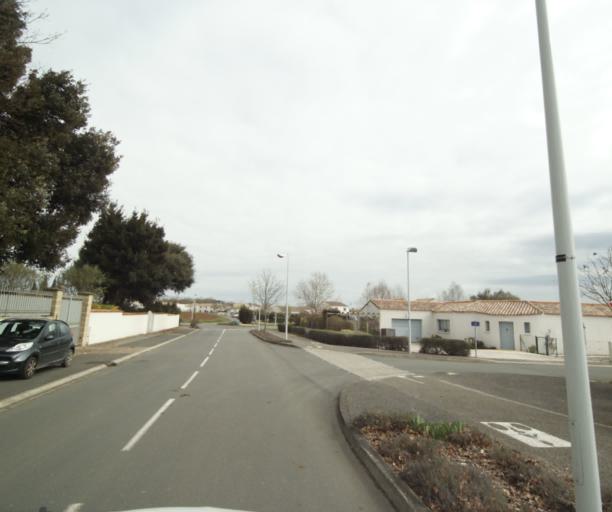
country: FR
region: Poitou-Charentes
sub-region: Departement de la Charente-Maritime
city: Lagord
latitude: 46.1878
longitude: -1.1627
